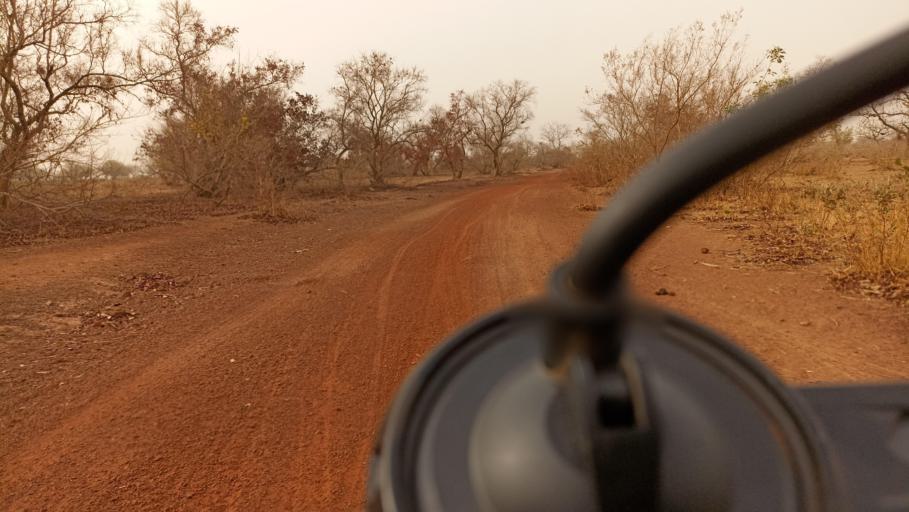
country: BF
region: Nord
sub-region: Province du Zondoma
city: Gourcy
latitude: 13.1548
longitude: -2.5948
